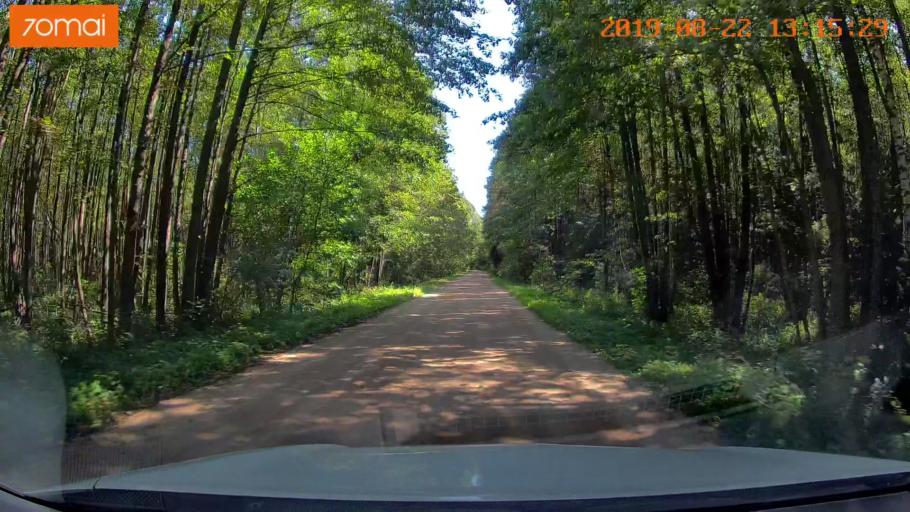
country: BY
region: Minsk
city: Prawdzinski
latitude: 53.2598
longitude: 27.8973
